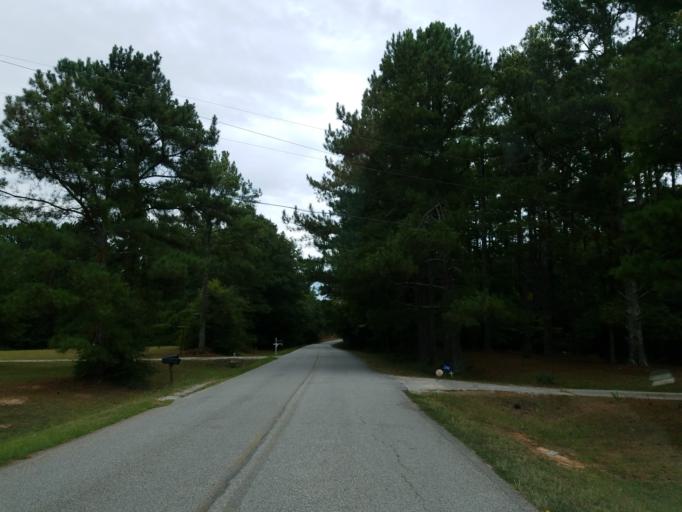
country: US
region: Georgia
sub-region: Clayton County
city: Lovejoy
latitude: 33.4215
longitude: -84.3120
